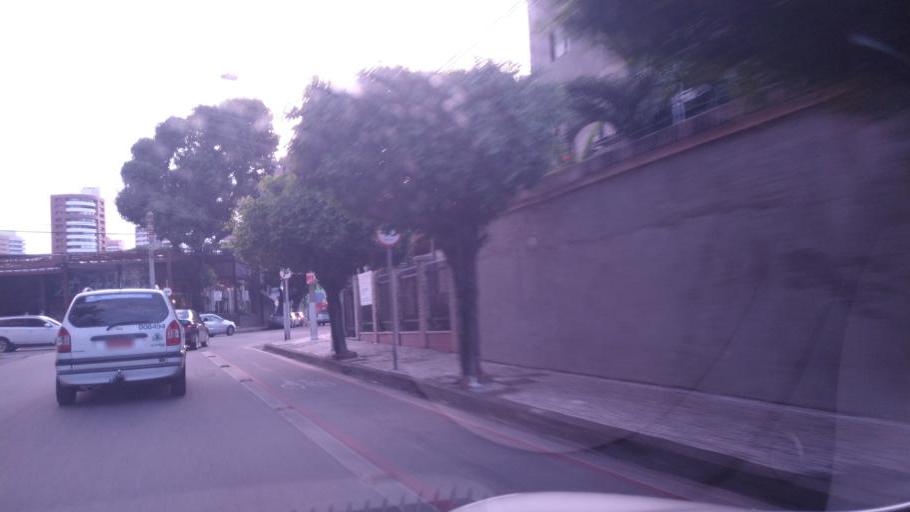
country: BR
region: Ceara
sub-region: Fortaleza
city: Fortaleza
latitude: -3.7316
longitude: -38.4890
